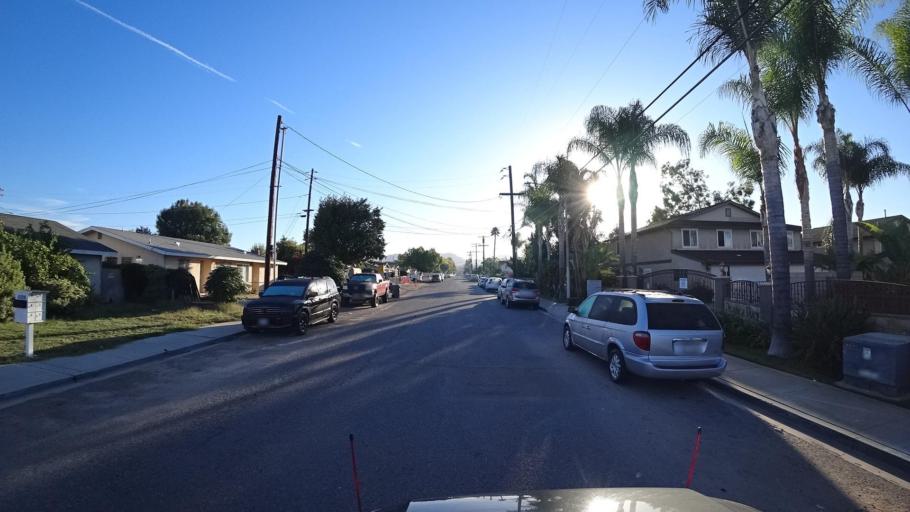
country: US
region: California
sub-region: San Diego County
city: Bostonia
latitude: 32.8116
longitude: -116.9433
